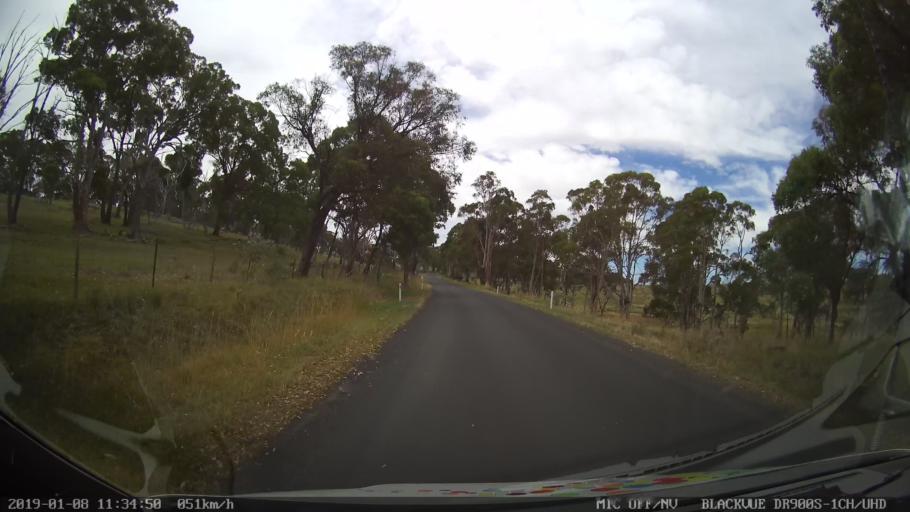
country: AU
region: New South Wales
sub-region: Guyra
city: Guyra
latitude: -30.3323
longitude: 151.5355
